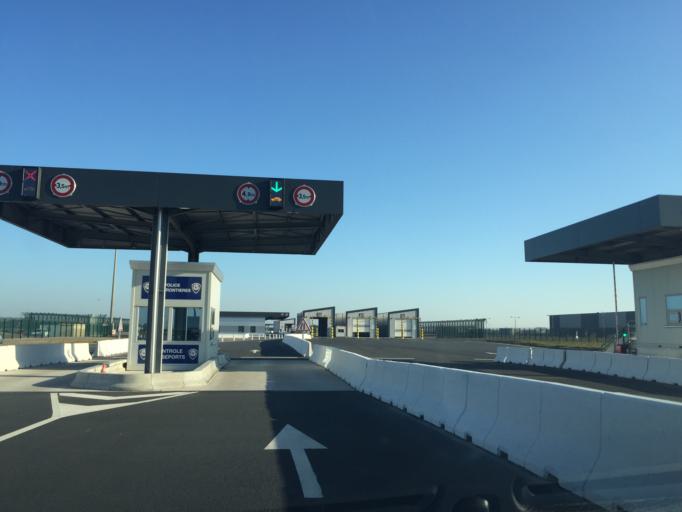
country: FR
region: Nord-Pas-de-Calais
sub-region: Departement du Nord
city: Loon-Plage
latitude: 51.0169
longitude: 2.1986
